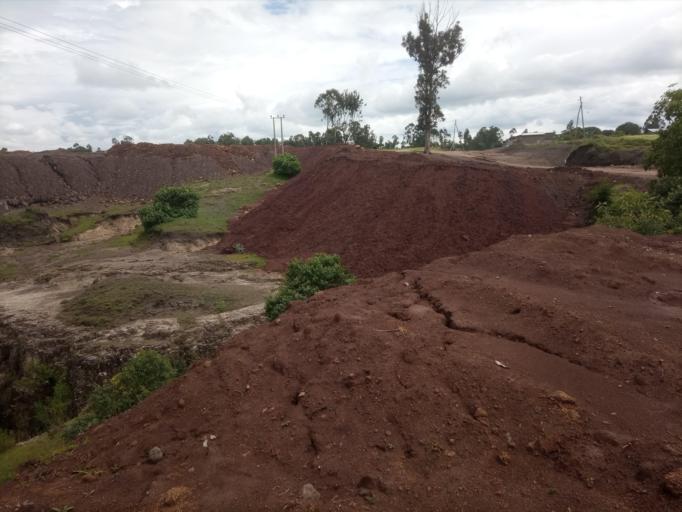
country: ET
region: Southern Nations, Nationalities, and People's Region
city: K'olito
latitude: 7.4453
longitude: 37.8418
